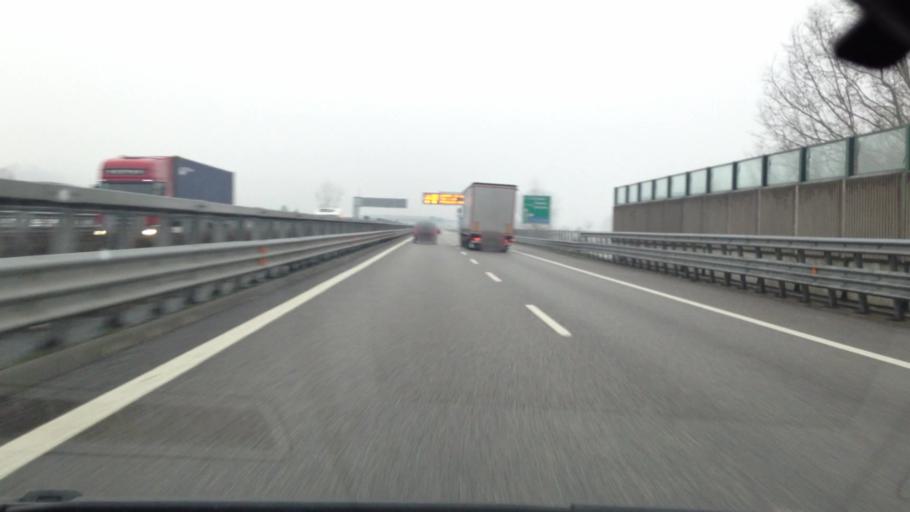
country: IT
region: Piedmont
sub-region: Provincia di Asti
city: Mongardino
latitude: 44.8542
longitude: 8.1977
